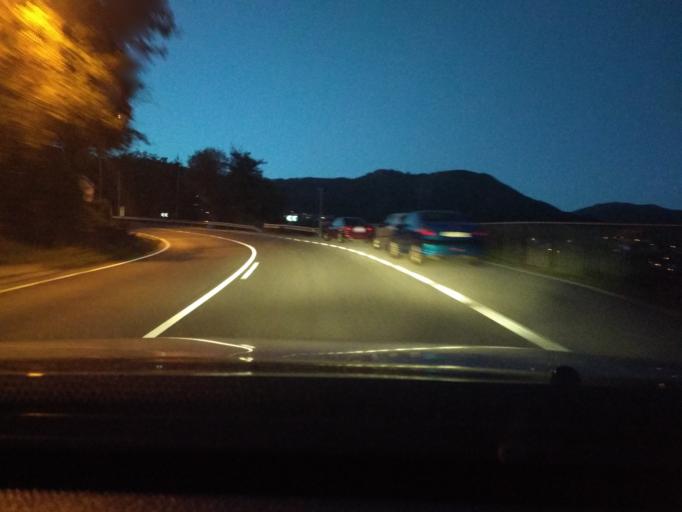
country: ES
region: Galicia
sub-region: Provincia de Pontevedra
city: Moana
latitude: 42.2976
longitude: -8.7413
